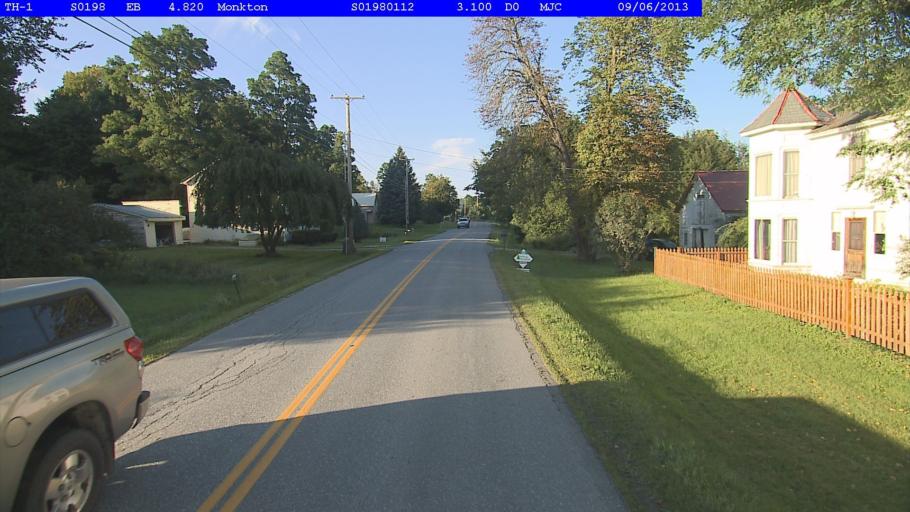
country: US
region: Vermont
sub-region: Chittenden County
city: Hinesburg
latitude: 44.2382
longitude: -73.1441
